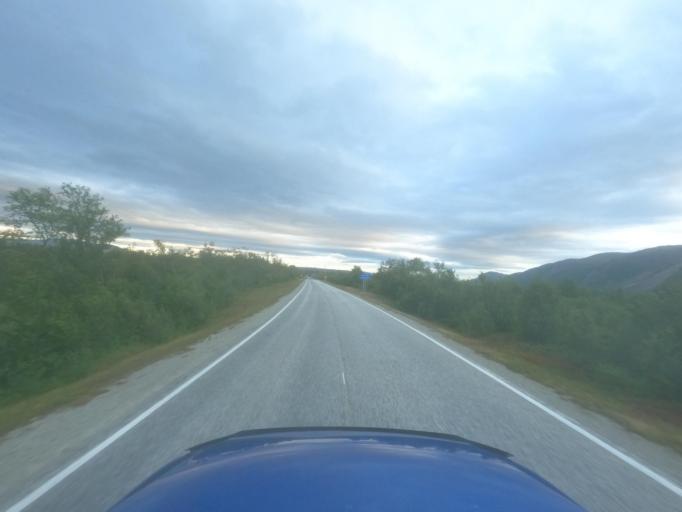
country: NO
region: Finnmark Fylke
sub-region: Porsanger
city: Lakselv
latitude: 70.0631
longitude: 24.9291
